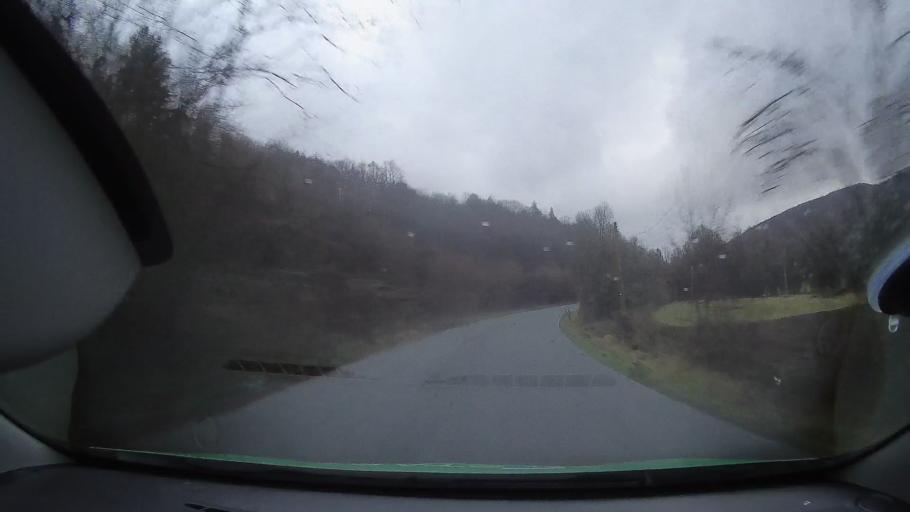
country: RO
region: Hunedoara
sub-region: Comuna Baia de Cris
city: Baia de Cris
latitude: 46.2064
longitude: 22.7165
